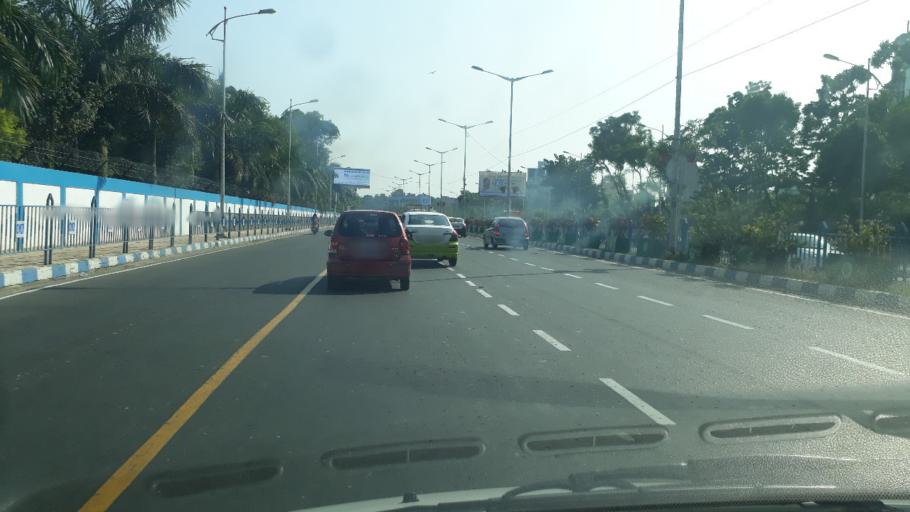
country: IN
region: West Bengal
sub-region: Kolkata
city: Kolkata
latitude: 22.5645
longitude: 88.4072
